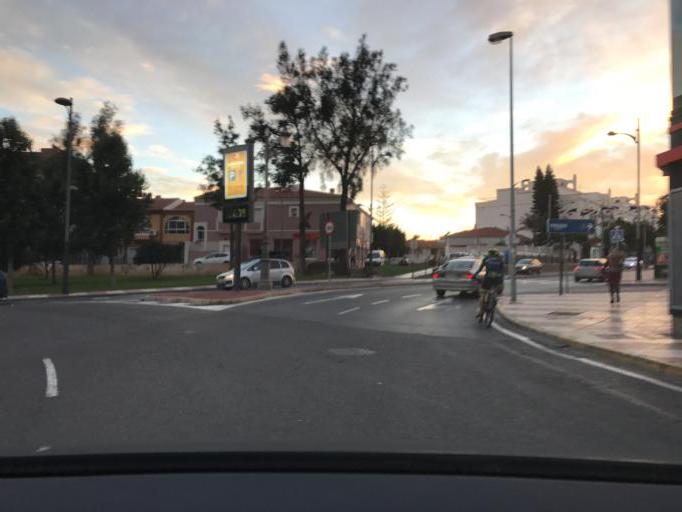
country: ES
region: Andalusia
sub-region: Provincia de Almeria
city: Aguadulce
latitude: 36.8128
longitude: -2.5789
